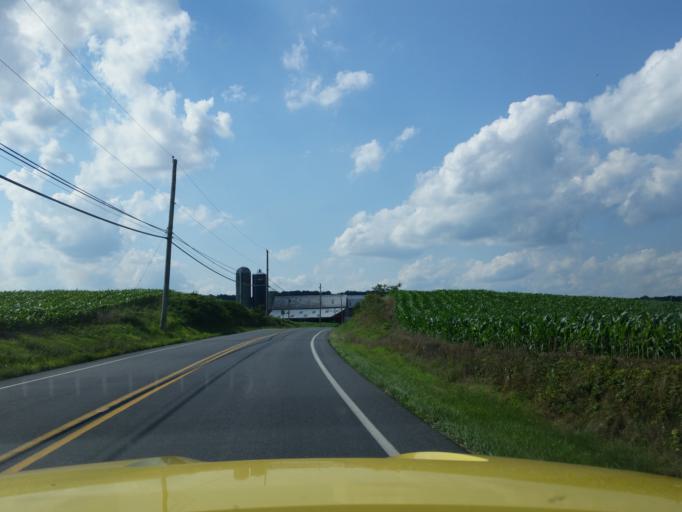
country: US
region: Pennsylvania
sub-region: Lancaster County
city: Mount Joy
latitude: 40.2098
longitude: -76.5054
